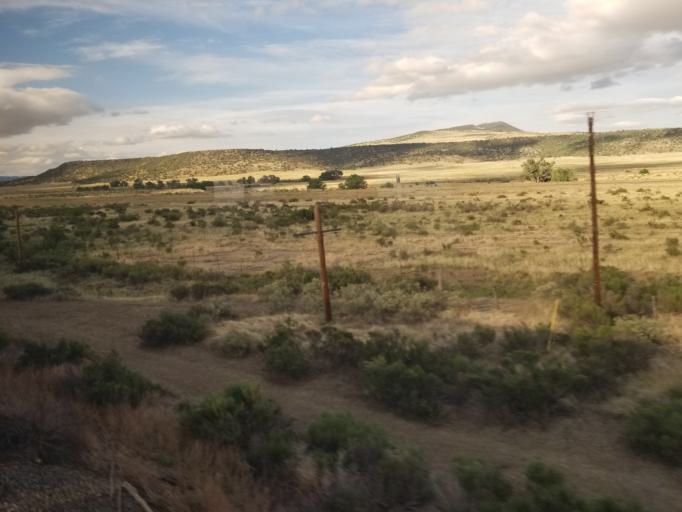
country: US
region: New Mexico
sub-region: Colfax County
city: Raton
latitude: 36.6679
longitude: -104.4976
